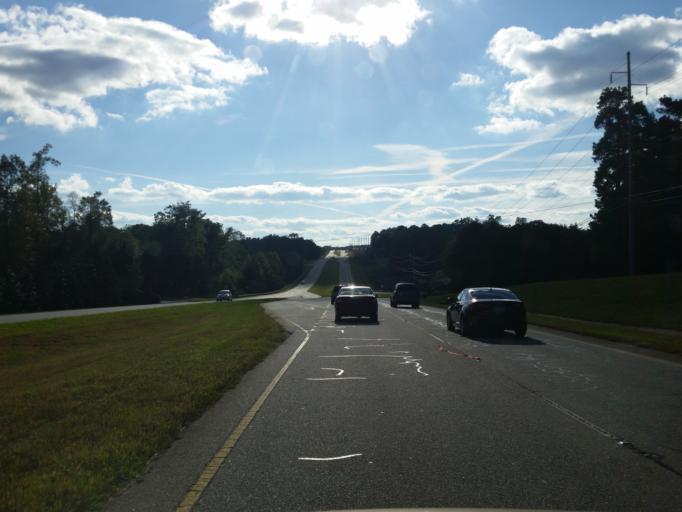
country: US
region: Georgia
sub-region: Paulding County
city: Hiram
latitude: 33.9246
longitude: -84.7518
